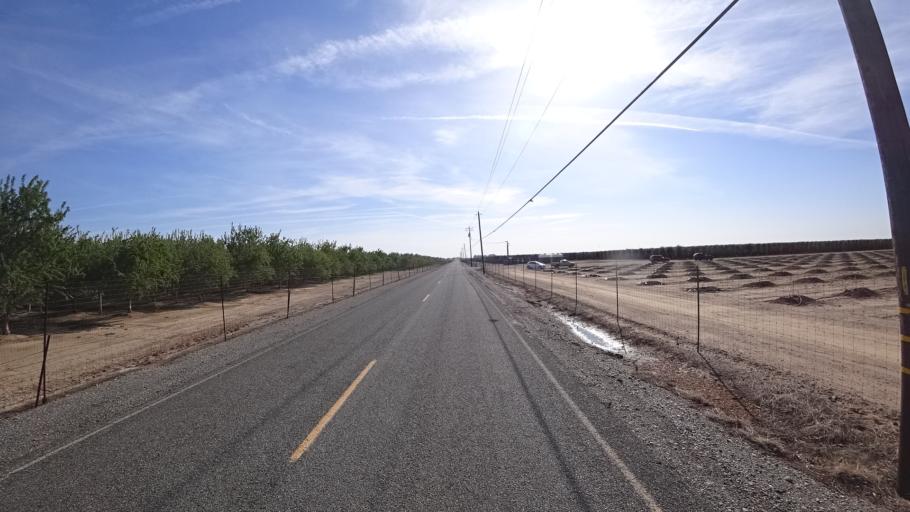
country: US
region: California
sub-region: Glenn County
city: Orland
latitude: 39.6679
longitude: -122.2134
